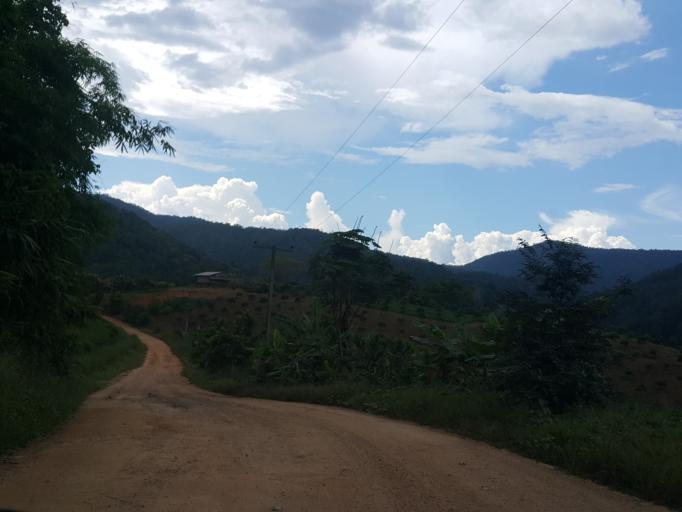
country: TH
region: Chiang Mai
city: Phrao
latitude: 19.3292
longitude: 99.1377
